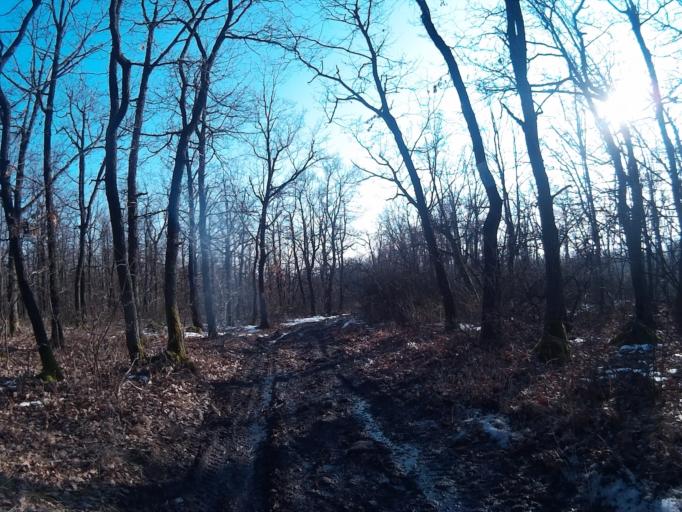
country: HU
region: Nograd
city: Paszto
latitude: 47.9393
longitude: 19.6324
